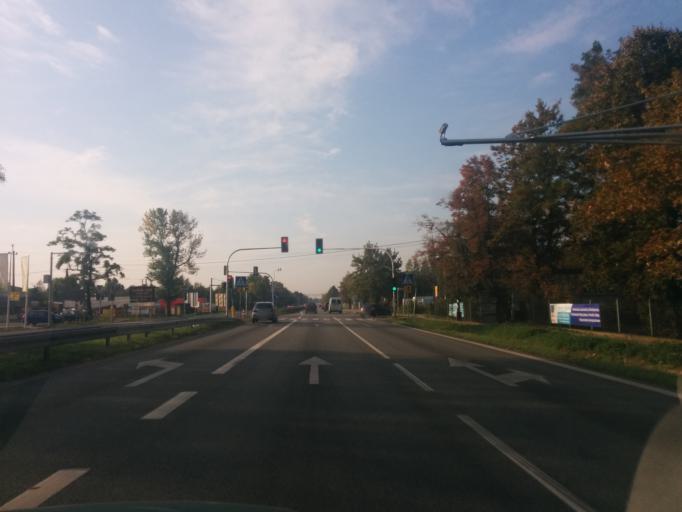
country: PL
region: Masovian Voivodeship
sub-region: Powiat piaseczynski
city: Tarczyn
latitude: 52.0394
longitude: 20.8614
